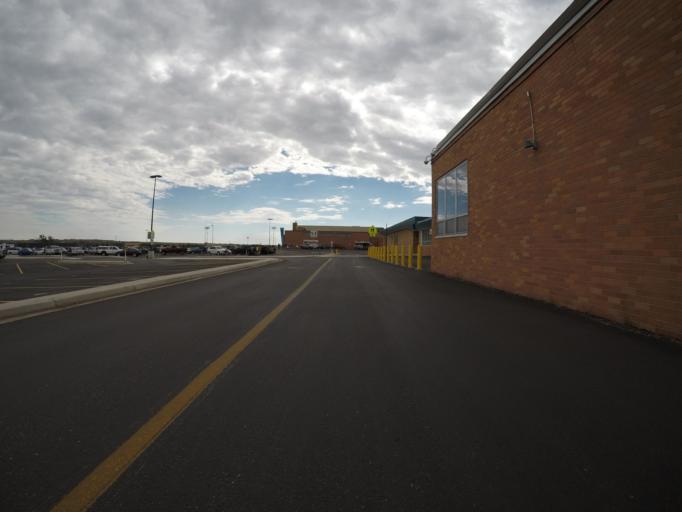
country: US
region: Wyoming
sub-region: Laramie County
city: Fox Farm-College
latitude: 41.1474
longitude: -104.7791
